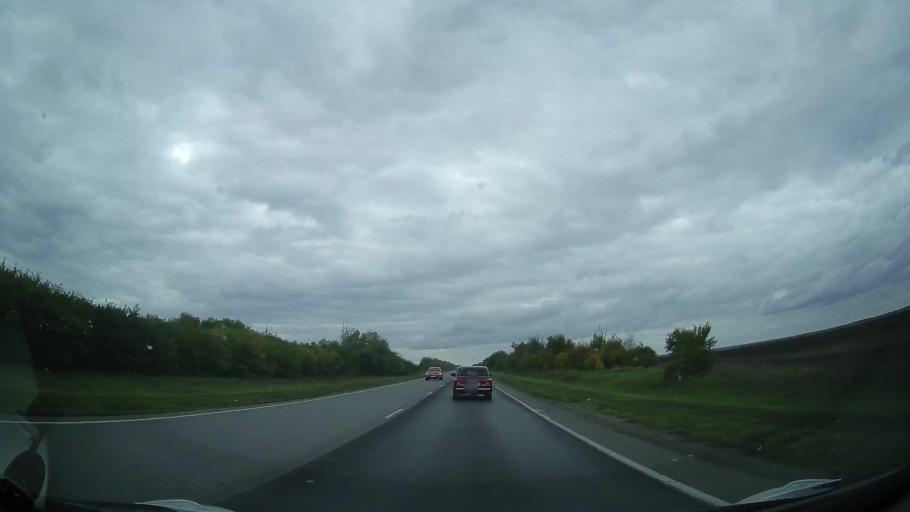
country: RU
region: Rostov
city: Yegorlykskaya
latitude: 46.5462
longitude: 40.7598
